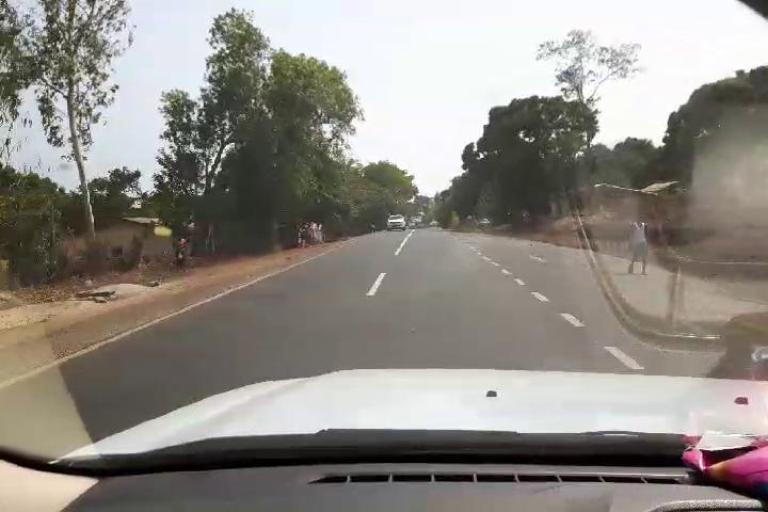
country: SL
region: Western Area
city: Waterloo
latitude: 8.2028
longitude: -13.1158
